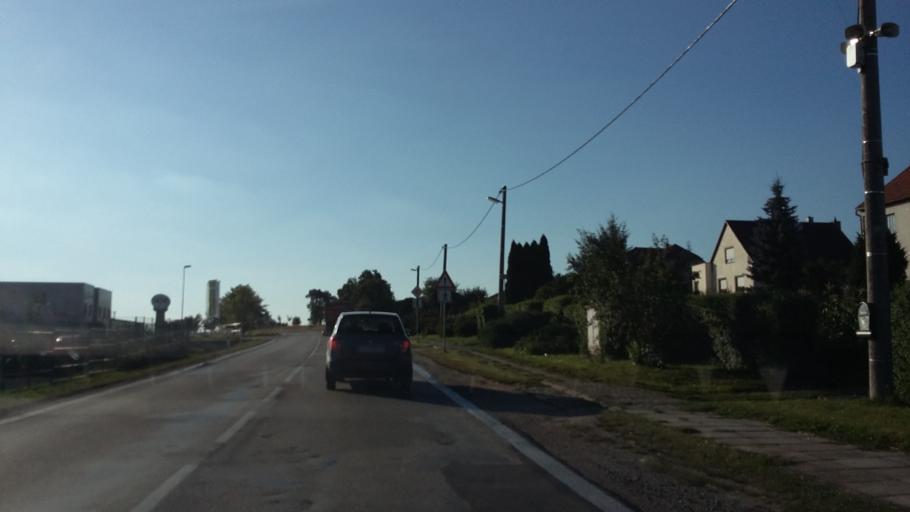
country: CZ
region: Vysocina
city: Merin
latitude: 49.3813
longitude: 15.9249
